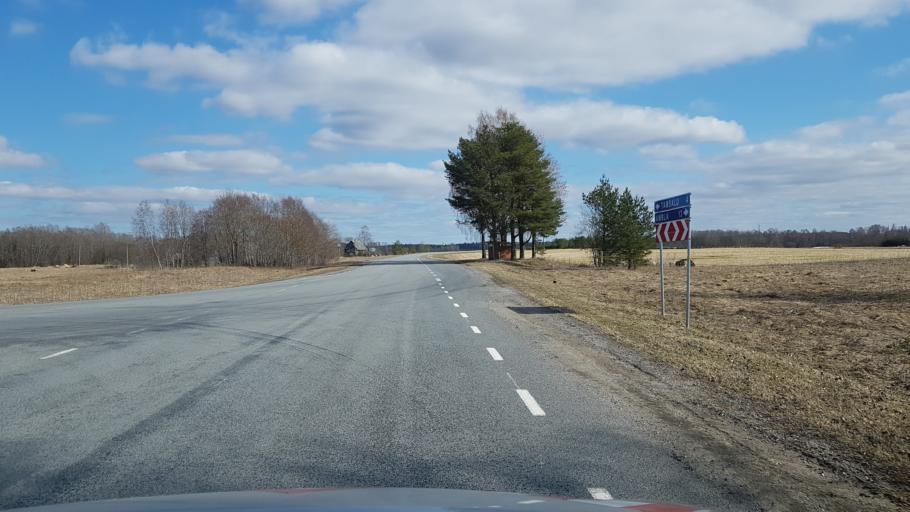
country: EE
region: Laeaene-Virumaa
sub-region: Tamsalu vald
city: Tamsalu
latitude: 59.1859
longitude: 26.0357
